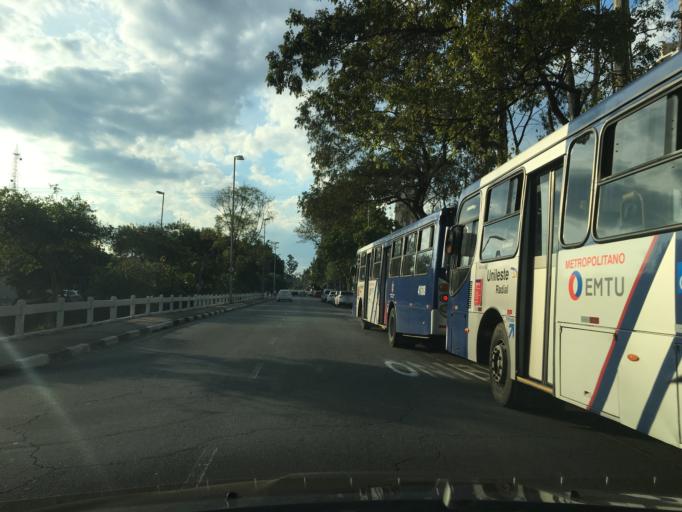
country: BR
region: Sao Paulo
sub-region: Guarulhos
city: Guarulhos
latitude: -23.4652
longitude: -46.5359
